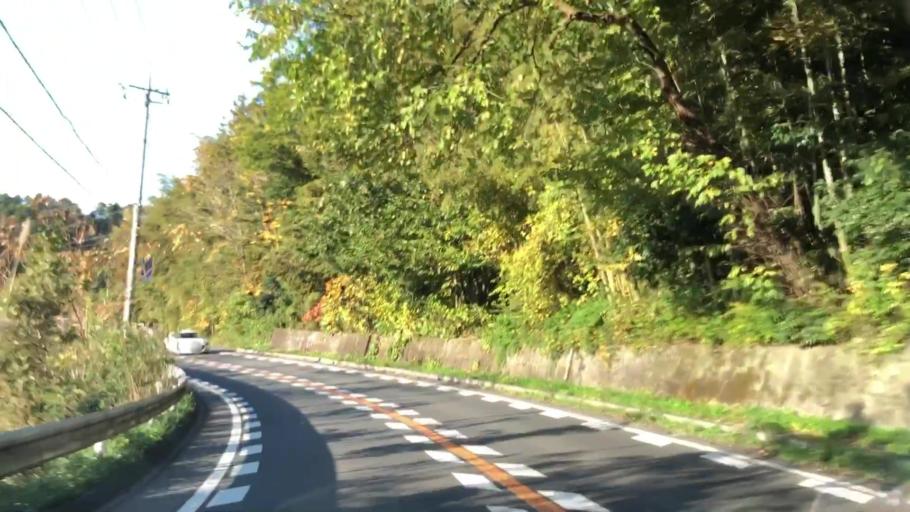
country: JP
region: Ibaraki
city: Tomobe
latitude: 36.4440
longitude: 140.3625
